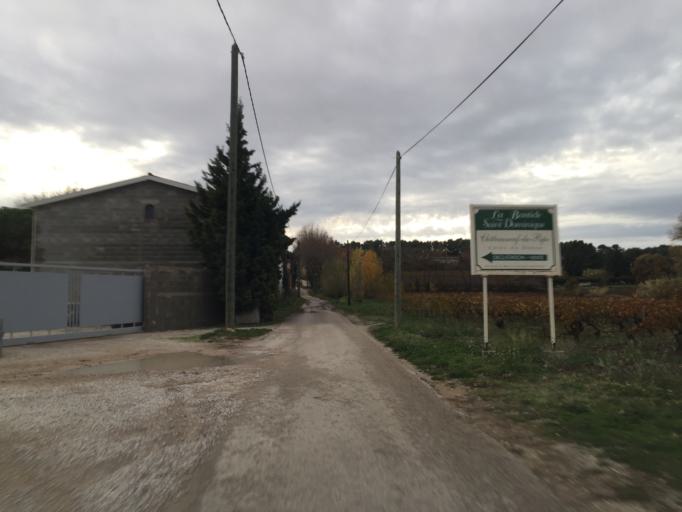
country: FR
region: Provence-Alpes-Cote d'Azur
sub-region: Departement du Vaucluse
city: Courthezon
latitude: 44.0854
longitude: 4.8611
